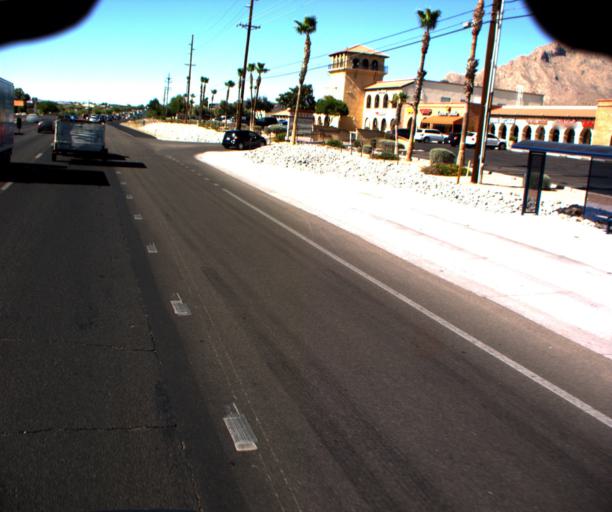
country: US
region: Arizona
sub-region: Pima County
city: Casas Adobes
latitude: 32.3383
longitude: -110.9773
